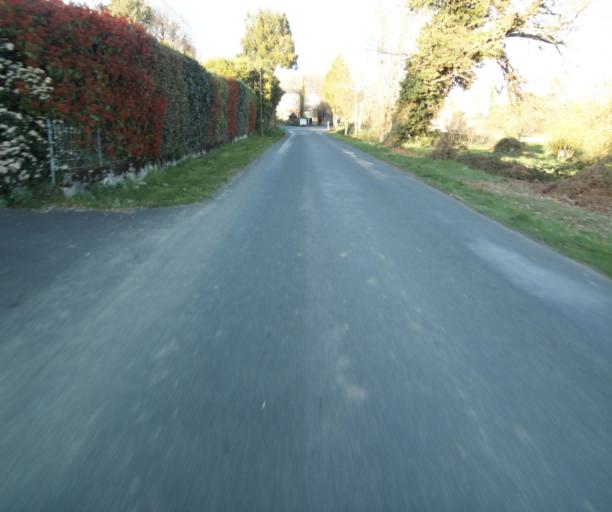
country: FR
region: Limousin
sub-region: Departement de la Correze
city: Saint-Mexant
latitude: 45.3318
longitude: 1.6094
